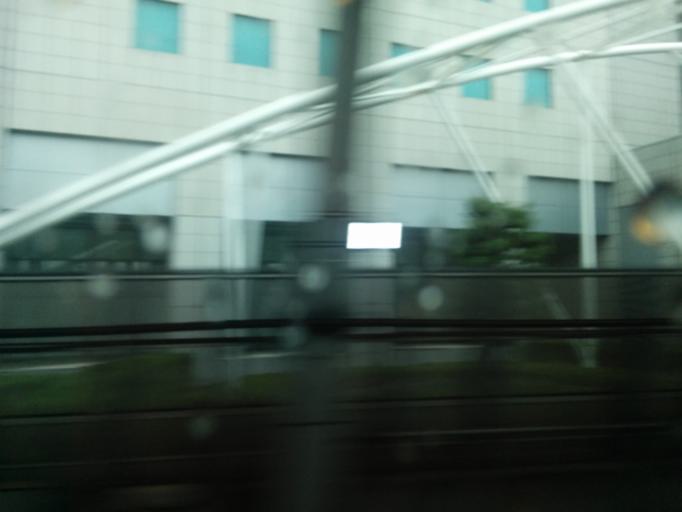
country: JP
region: Tokyo
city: Tokyo
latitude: 35.6331
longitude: 139.7418
